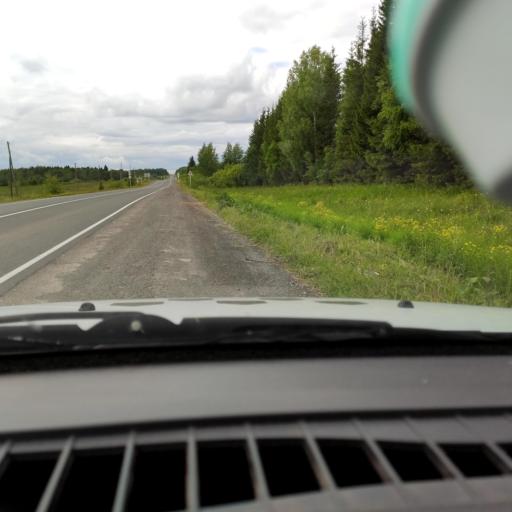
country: RU
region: Perm
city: Lys'va
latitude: 58.1639
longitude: 57.7773
